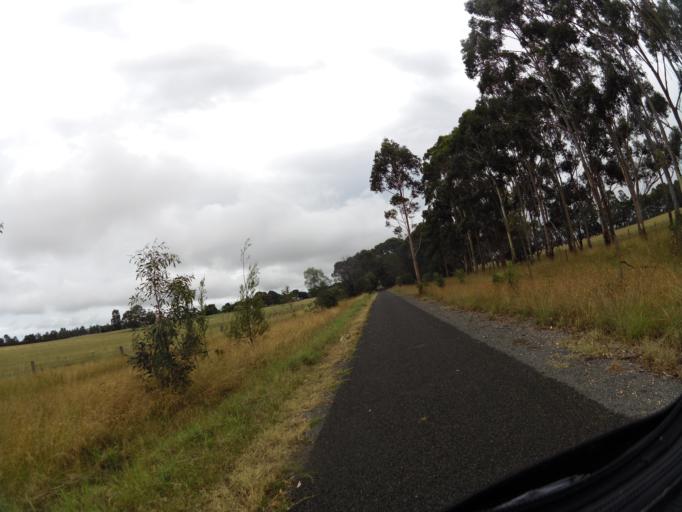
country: AU
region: Victoria
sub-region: East Gippsland
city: Bairnsdale
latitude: -37.8228
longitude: 147.7090
